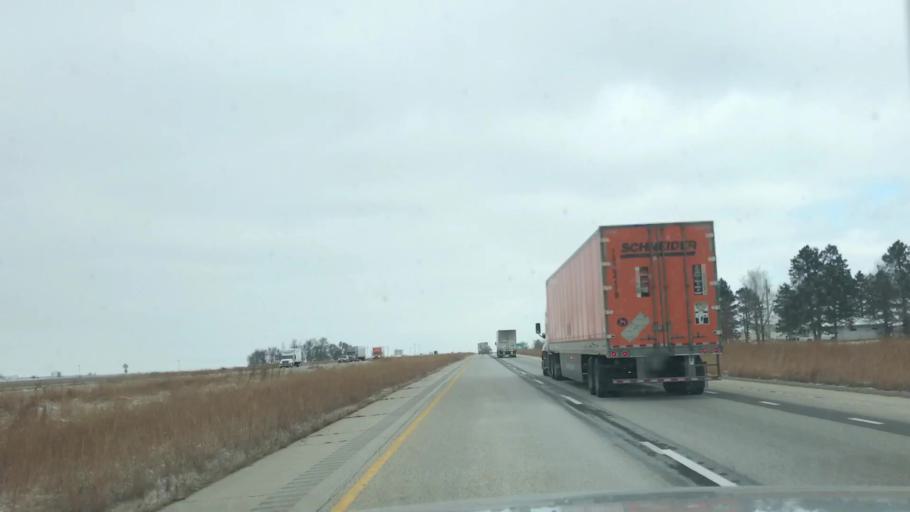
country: US
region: Illinois
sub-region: Sangamon County
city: Divernon
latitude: 39.4516
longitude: -89.6441
